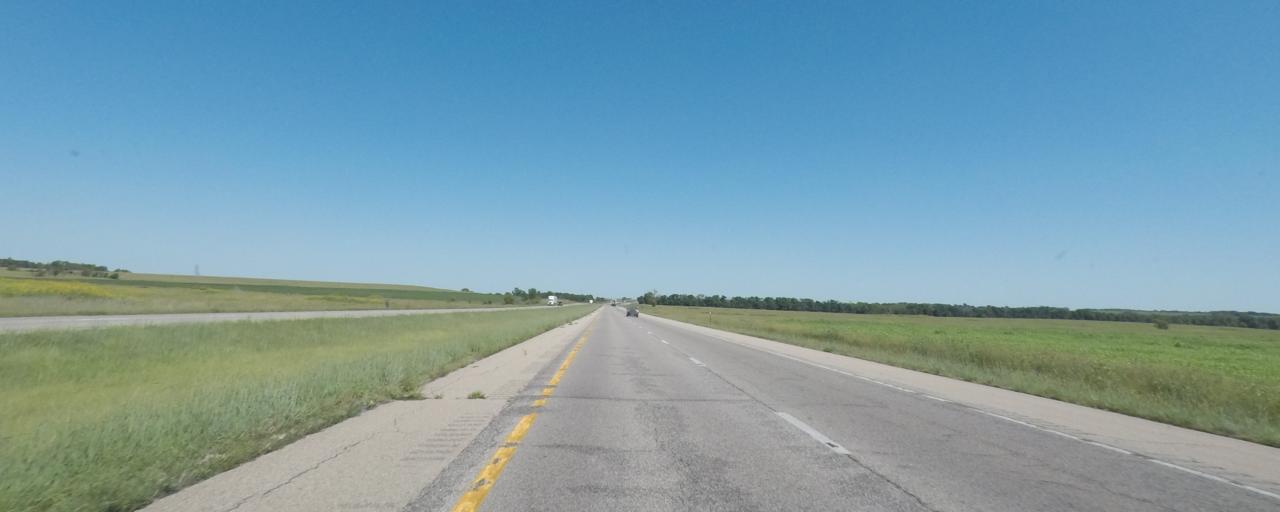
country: US
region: Kansas
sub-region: Osage County
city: Lyndon
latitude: 38.4265
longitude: -95.7803
